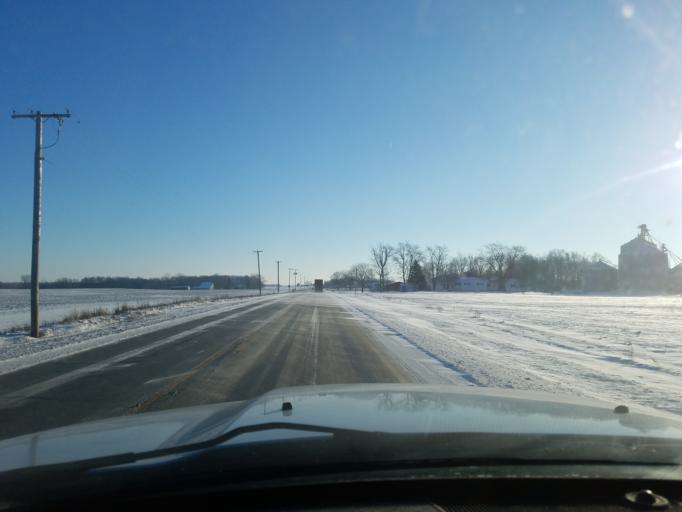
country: US
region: Indiana
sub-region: Noble County
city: Albion
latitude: 41.4530
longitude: -85.4713
